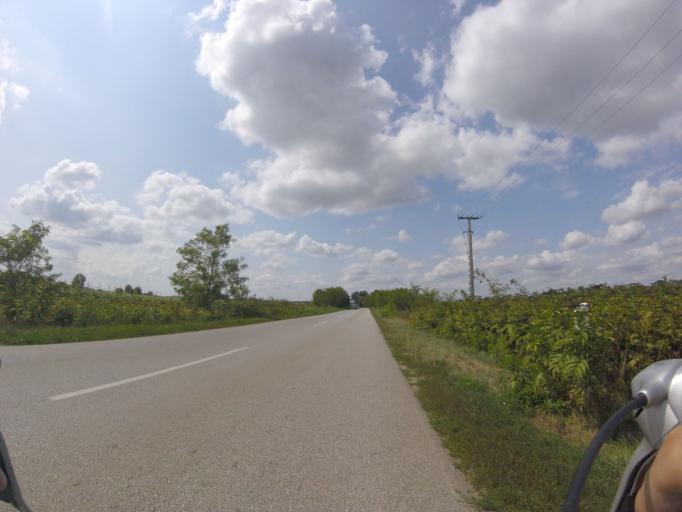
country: HU
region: Szabolcs-Szatmar-Bereg
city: Kemecse
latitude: 48.0675
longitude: 21.8164
